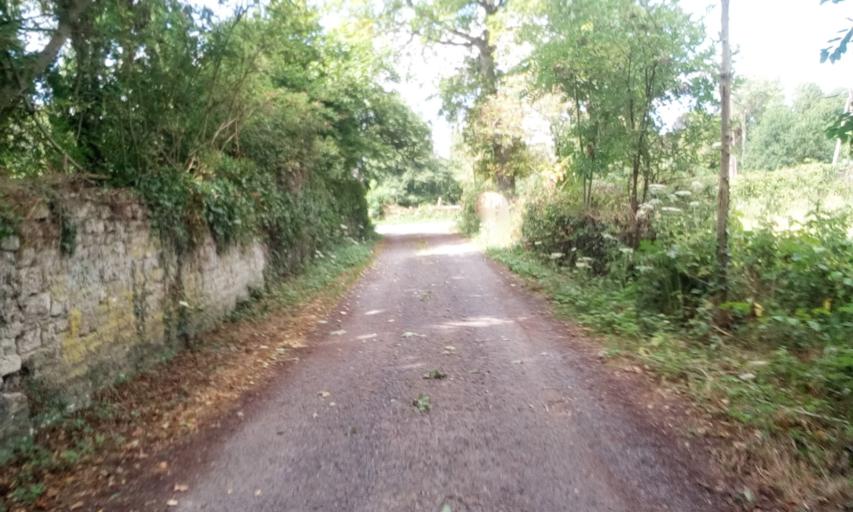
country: FR
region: Lower Normandy
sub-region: Departement du Calvados
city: Creully
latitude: 49.2917
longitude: -0.5122
